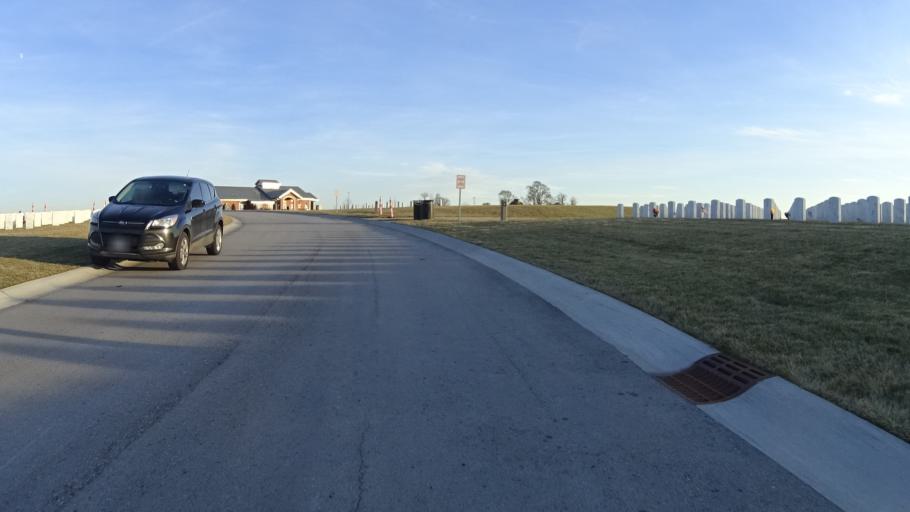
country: US
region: Nebraska
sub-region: Sarpy County
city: Chalco
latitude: 41.1354
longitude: -96.1340
